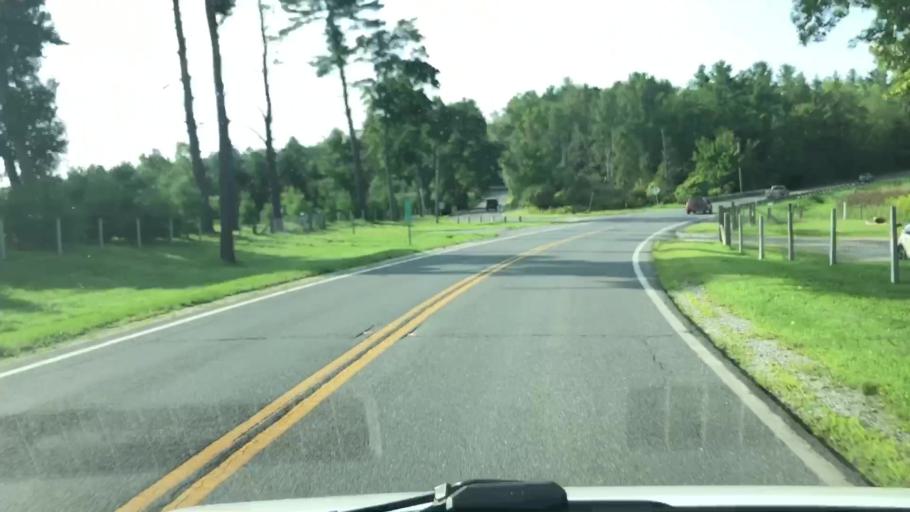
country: US
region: Massachusetts
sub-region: Berkshire County
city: Lee
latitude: 42.3146
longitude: -73.2860
